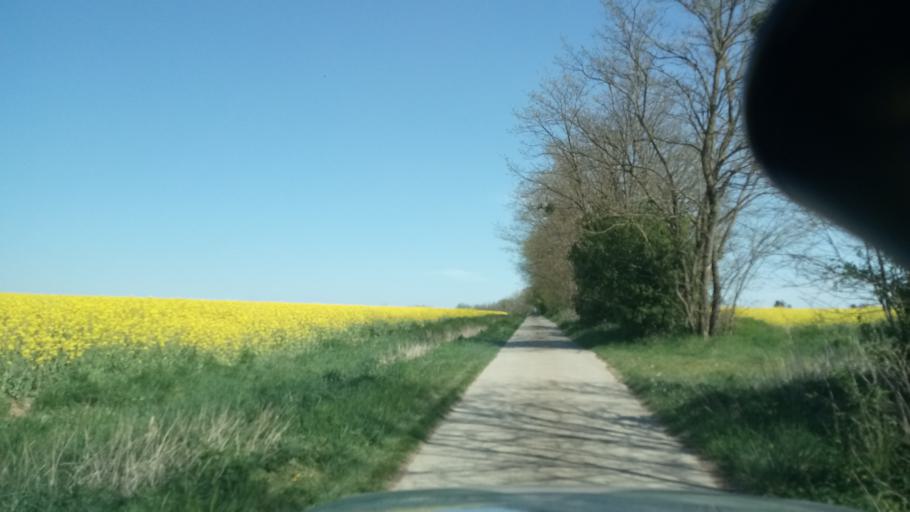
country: HU
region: Zala
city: Pacsa
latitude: 46.7040
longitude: 17.0900
